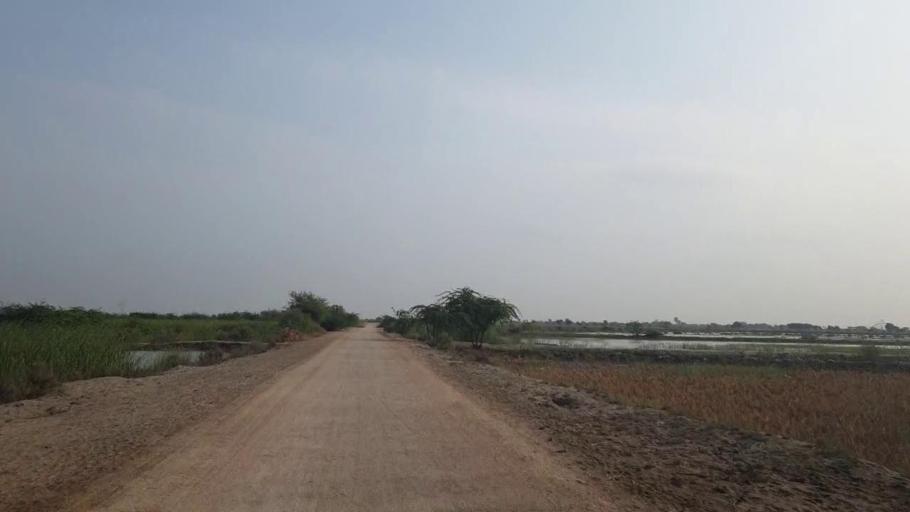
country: PK
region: Sindh
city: Badin
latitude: 24.6036
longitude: 68.6951
